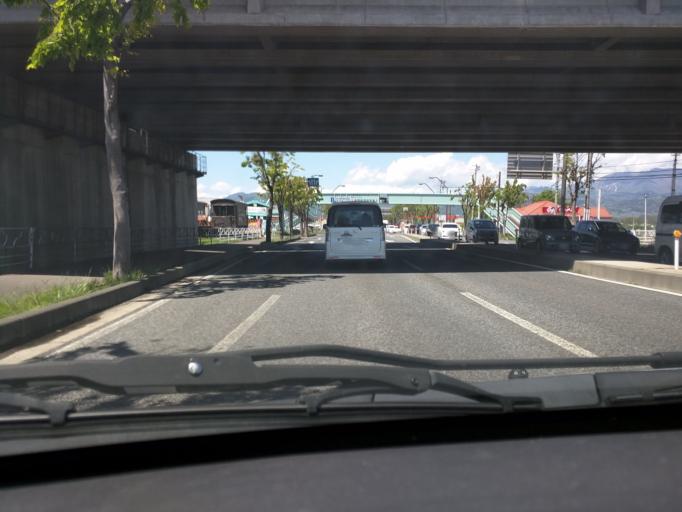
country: JP
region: Nagano
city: Suzaka
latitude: 36.6368
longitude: 138.2747
